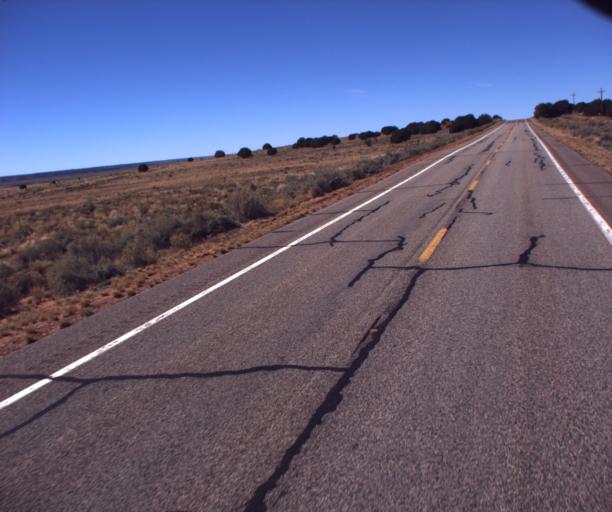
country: US
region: Arizona
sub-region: Mohave County
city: Colorado City
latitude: 36.8580
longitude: -112.7657
